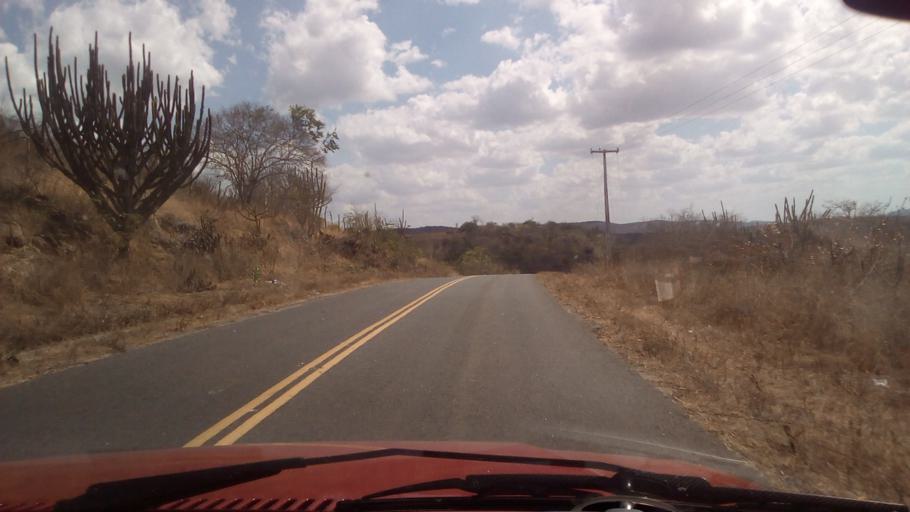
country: BR
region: Paraiba
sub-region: Cacimba De Dentro
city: Cacimba de Dentro
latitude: -6.6810
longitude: -35.7428
